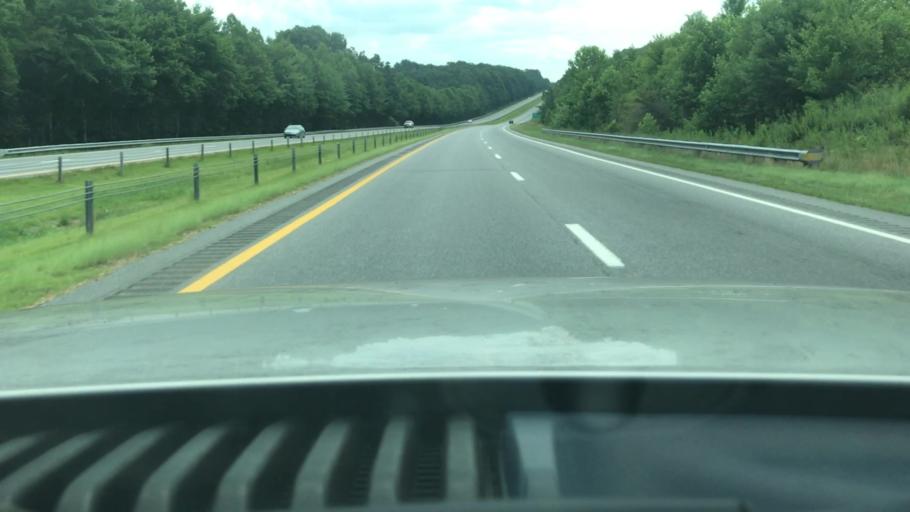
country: US
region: North Carolina
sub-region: Wilkes County
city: North Wilkesboro
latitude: 36.1440
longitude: -81.0602
